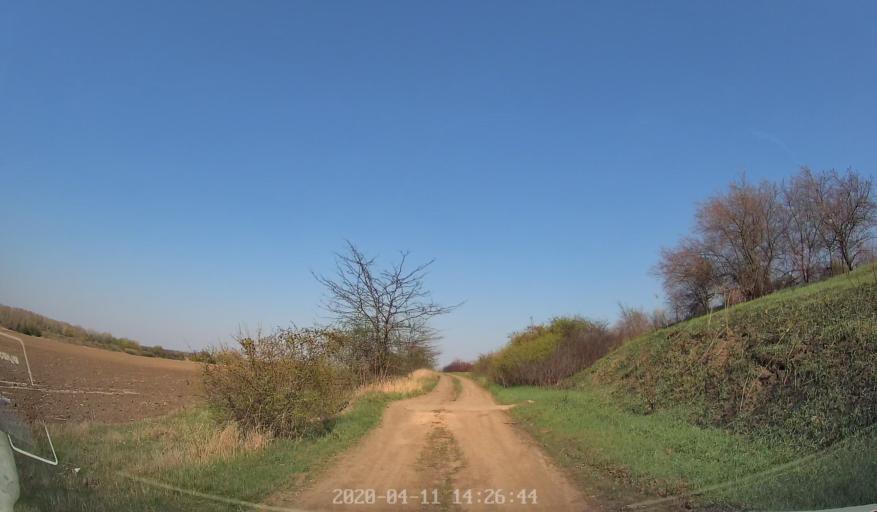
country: MD
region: Chisinau
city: Vadul lui Voda
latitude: 47.0951
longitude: 29.1492
